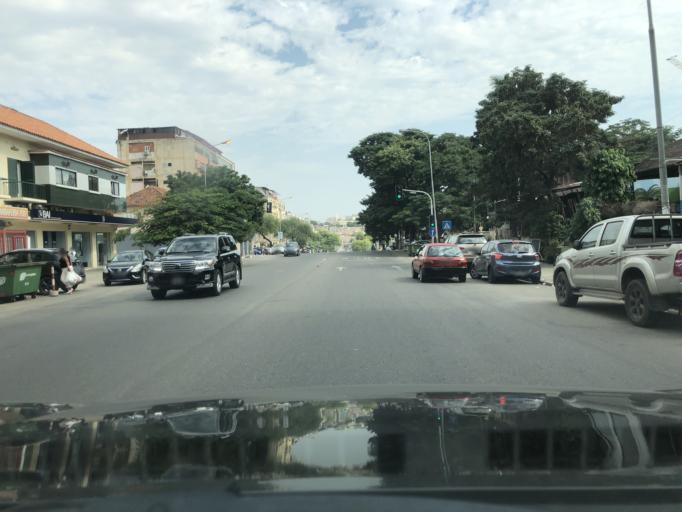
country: AO
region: Luanda
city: Luanda
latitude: -8.8252
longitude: 13.2280
